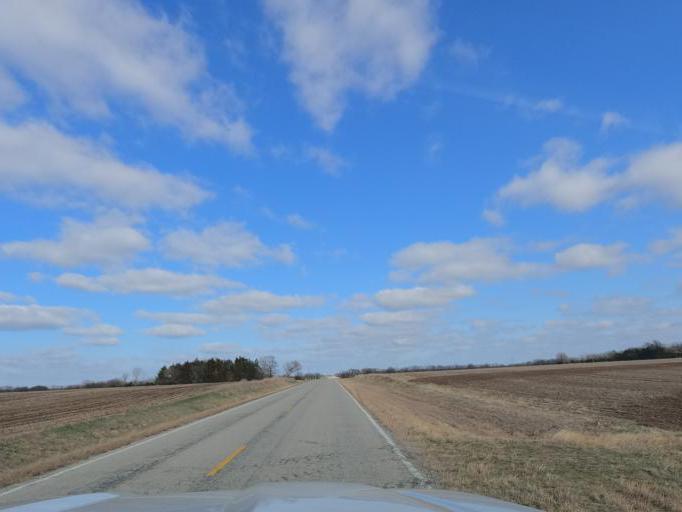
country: US
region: Kansas
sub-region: McPherson County
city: Inman
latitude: 38.2320
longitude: -97.8711
